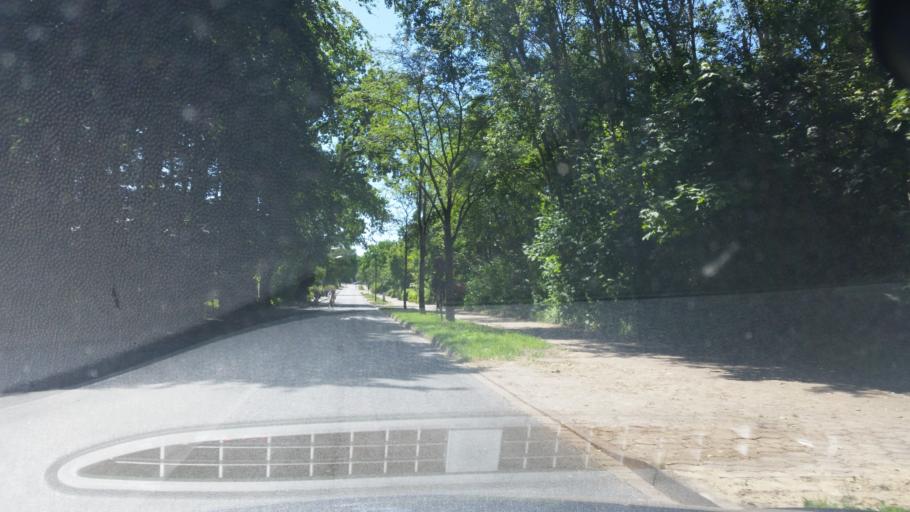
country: DE
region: Lower Saxony
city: Seevetal
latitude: 53.4134
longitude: 10.0253
